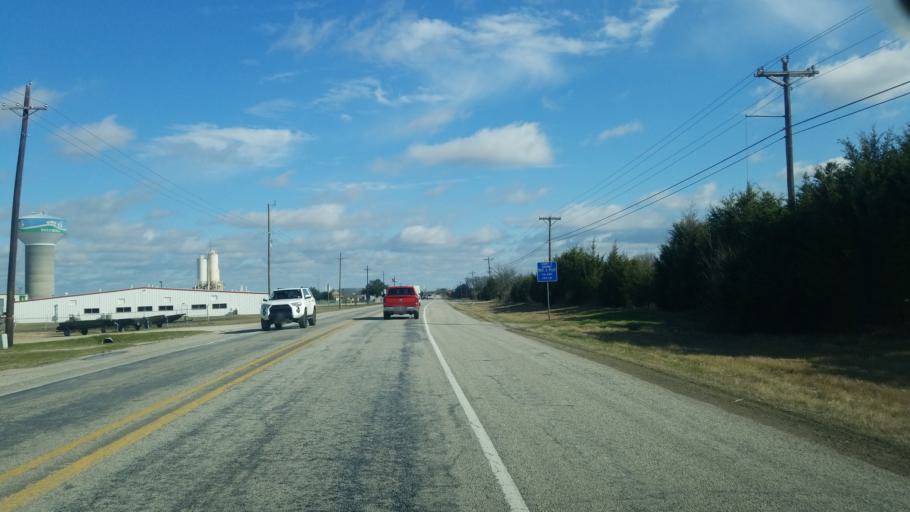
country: US
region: Texas
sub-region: Rockwall County
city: Fate
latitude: 32.9066
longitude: -96.4142
